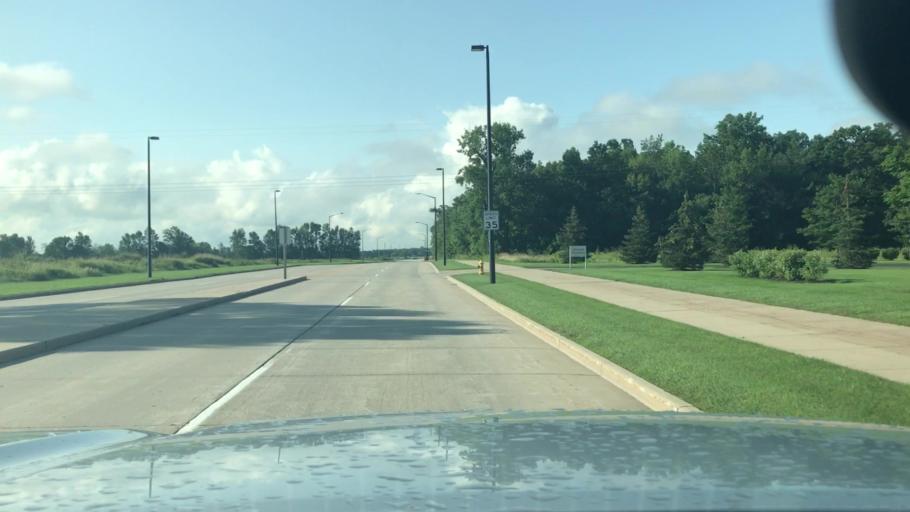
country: US
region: Wisconsin
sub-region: Brown County
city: Bellevue
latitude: 44.4773
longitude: -87.9174
